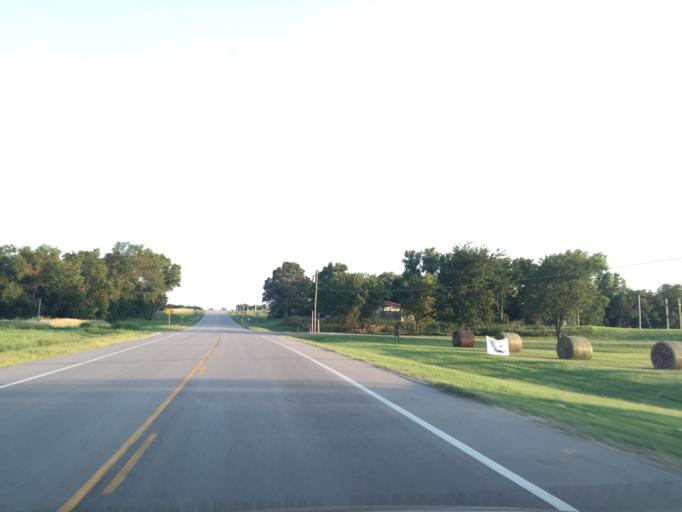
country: US
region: Kansas
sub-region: Ellsworth County
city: Ellsworth
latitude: 38.7251
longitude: -98.2345
